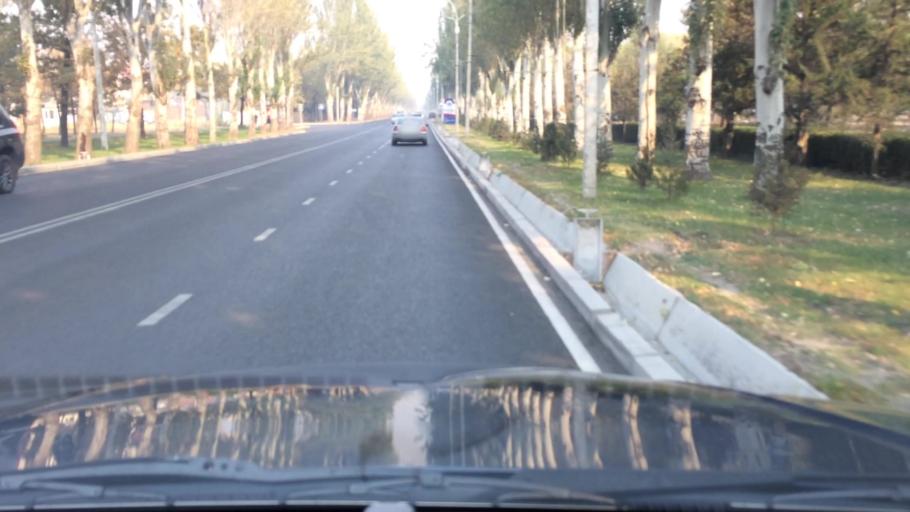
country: KG
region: Chuy
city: Bishkek
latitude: 42.8309
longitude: 74.5853
